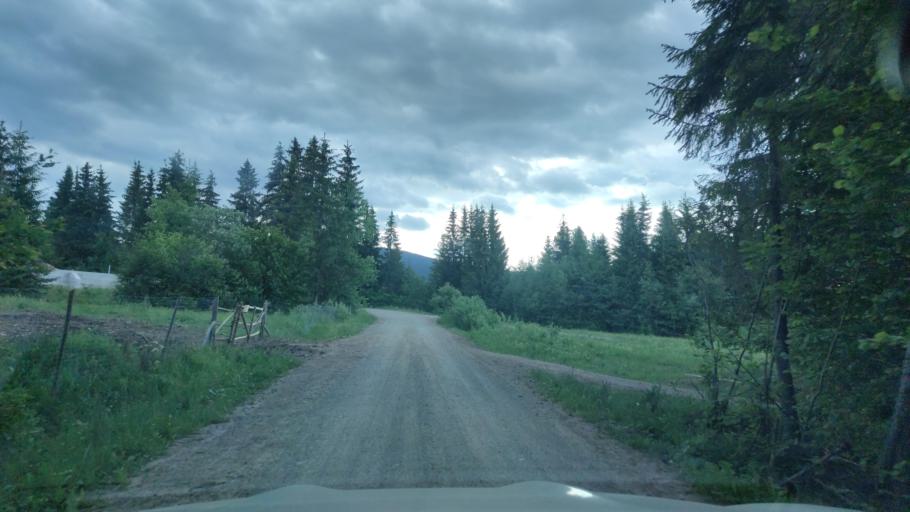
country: RO
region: Harghita
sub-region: Comuna Joseni
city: Joseni
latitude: 46.6678
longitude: 25.3785
